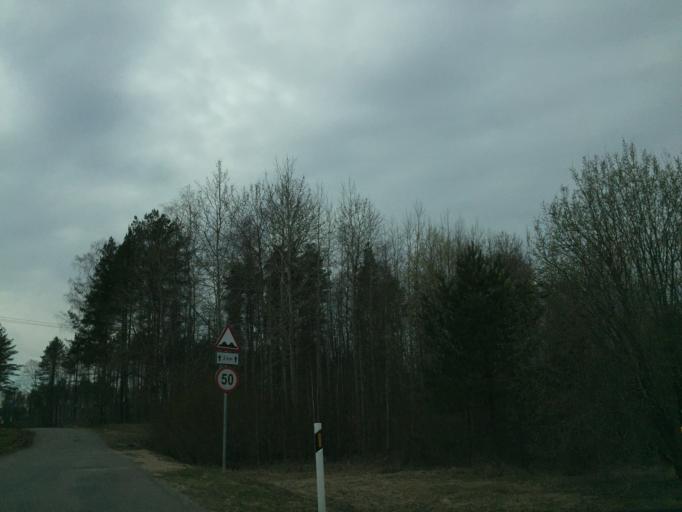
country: EE
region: Ida-Virumaa
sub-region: Narva-Joesuu linn
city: Narva-Joesuu
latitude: 59.4432
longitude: 28.1058
